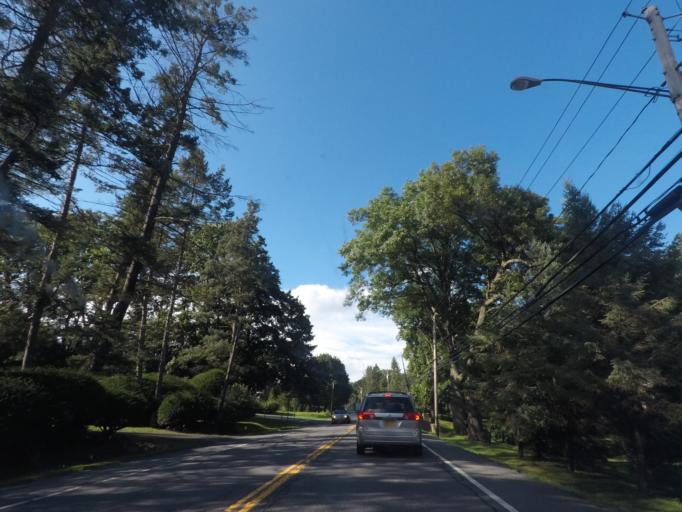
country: US
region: New York
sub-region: Albany County
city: West Albany
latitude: 42.6867
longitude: -73.7520
